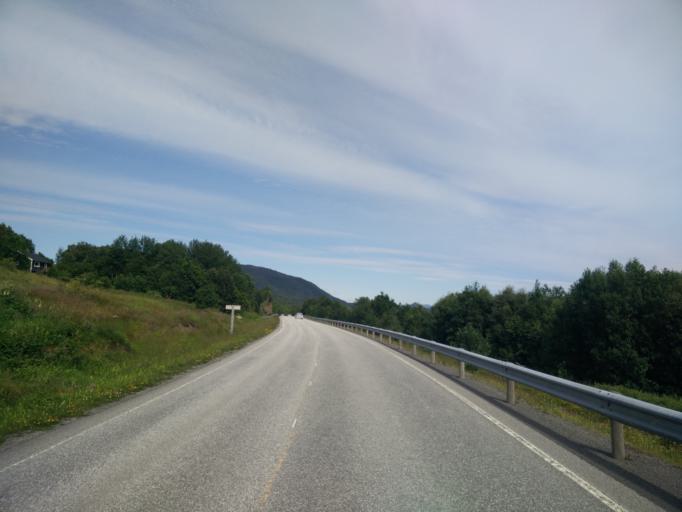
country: NO
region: More og Romsdal
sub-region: Kristiansund
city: Rensvik
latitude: 62.9767
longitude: 7.8610
